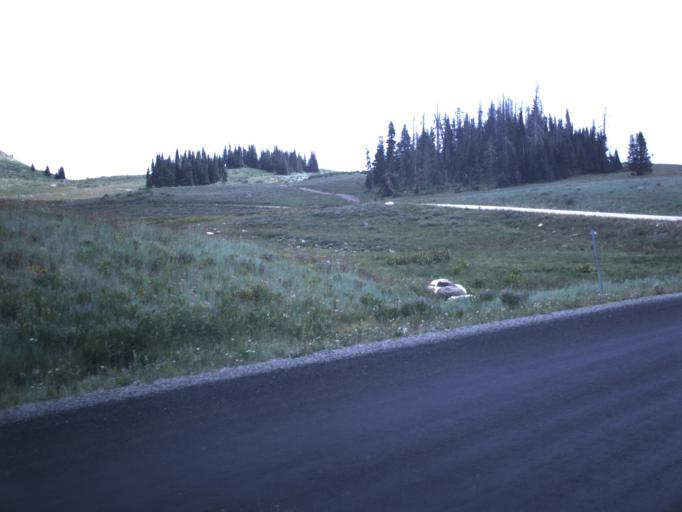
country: US
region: Utah
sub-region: Summit County
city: Francis
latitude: 40.4860
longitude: -111.0220
